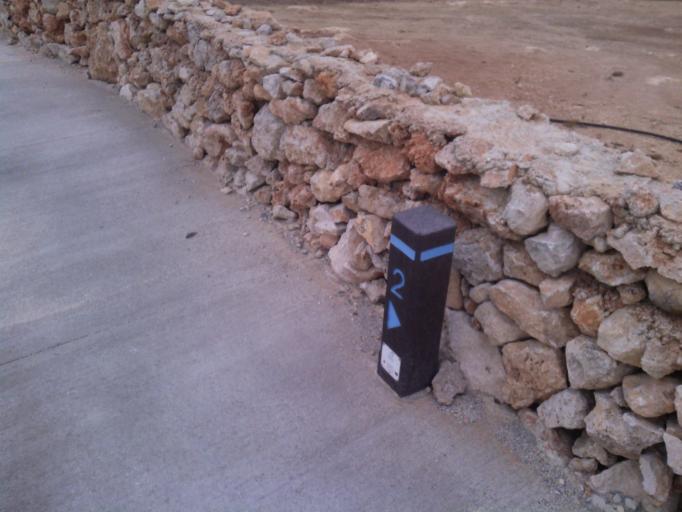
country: MT
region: Il-Mellieha
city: Mellieha
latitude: 35.9765
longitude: 14.3468
